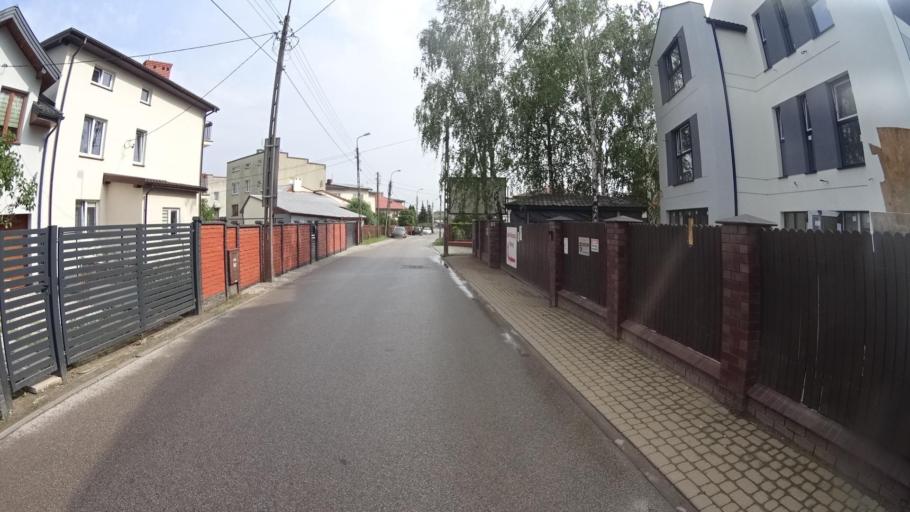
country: PL
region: Masovian Voivodeship
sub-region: Powiat pruszkowski
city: Raszyn
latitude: 52.1638
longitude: 20.9202
